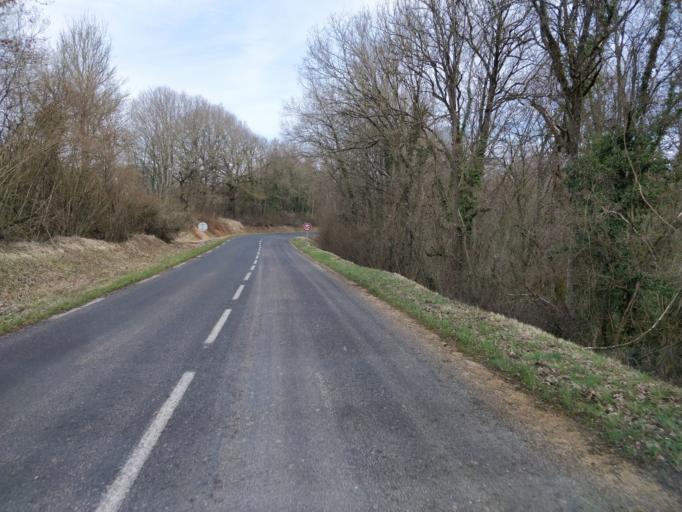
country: FR
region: Lorraine
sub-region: Departement de Meurthe-et-Moselle
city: Pagny-sur-Moselle
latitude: 48.9442
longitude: 5.8880
